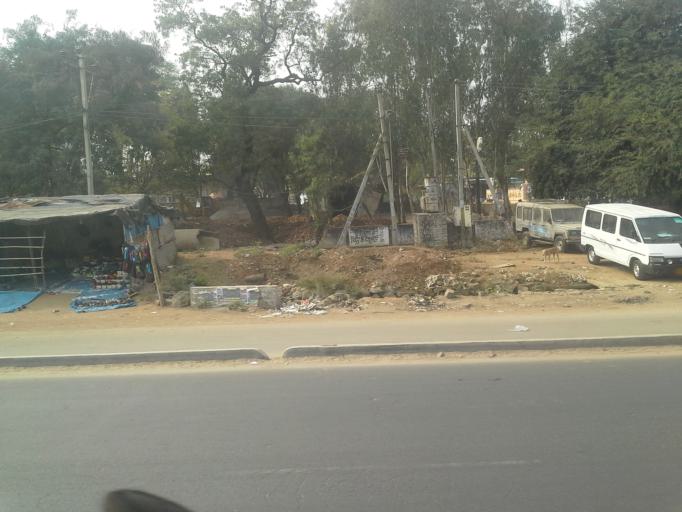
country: IN
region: Telangana
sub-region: Medak
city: Patancheru
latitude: 17.5291
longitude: 78.2661
